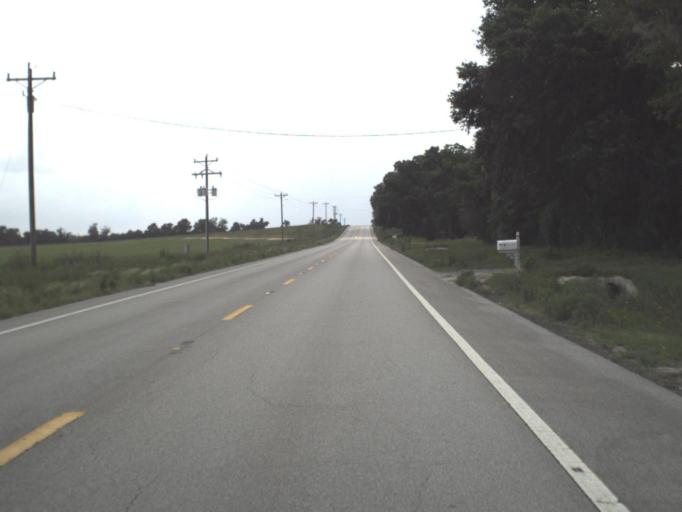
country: US
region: Florida
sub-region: Madison County
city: Madison
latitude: 30.4723
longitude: -83.3203
